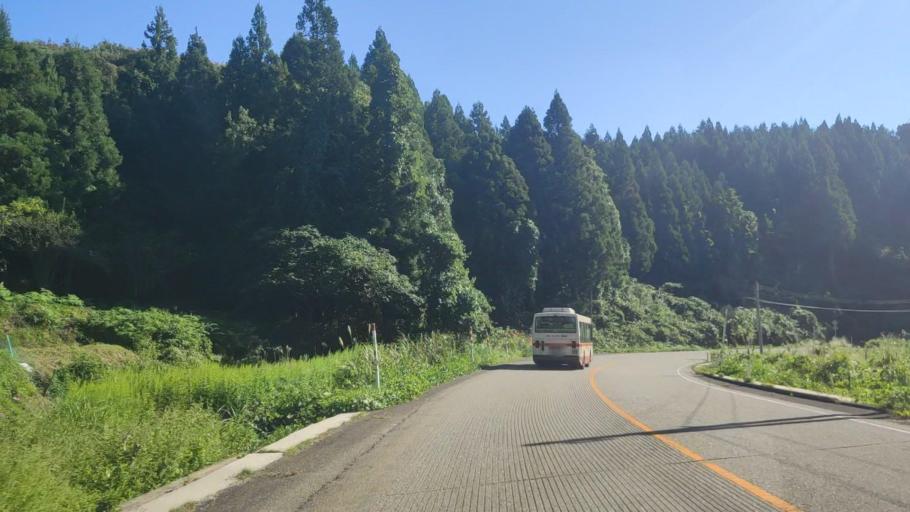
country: JP
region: Ishikawa
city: Nanao
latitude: 37.2425
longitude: 136.9880
